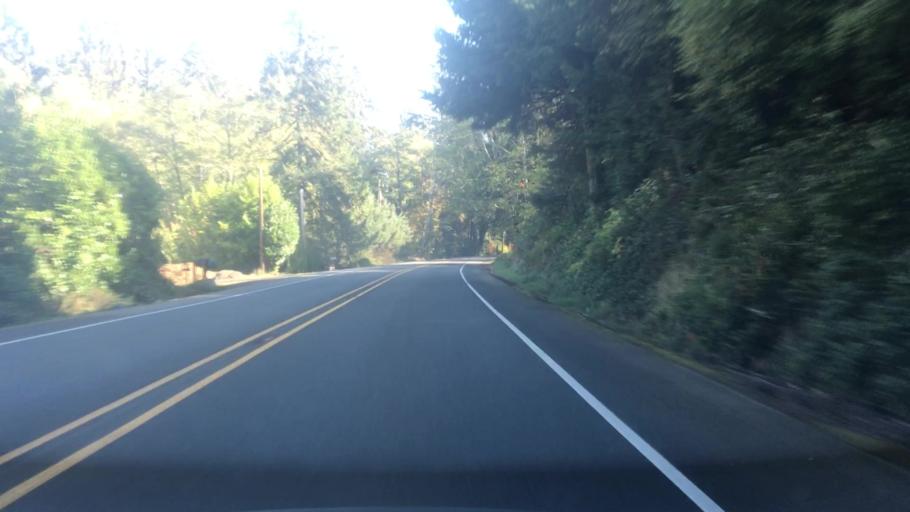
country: US
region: Oregon
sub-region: Lincoln County
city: Rose Lodge
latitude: 45.0059
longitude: -123.9147
